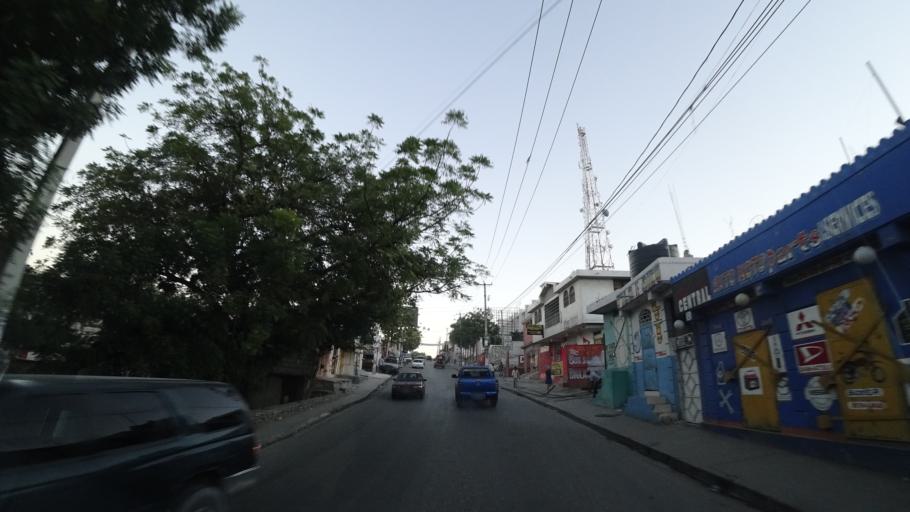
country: HT
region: Ouest
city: Delmas 73
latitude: 18.5490
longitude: -72.3169
